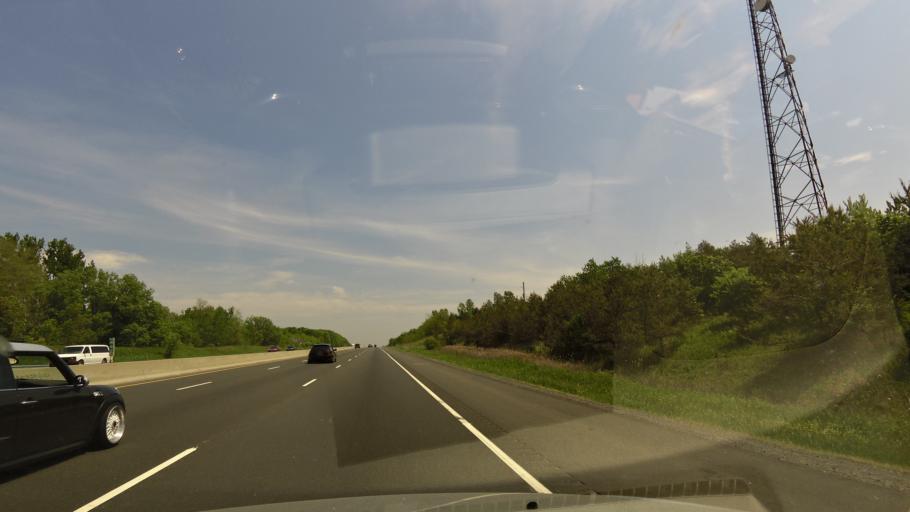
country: CA
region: Ontario
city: Oshawa
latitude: 43.9158
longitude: -78.5598
